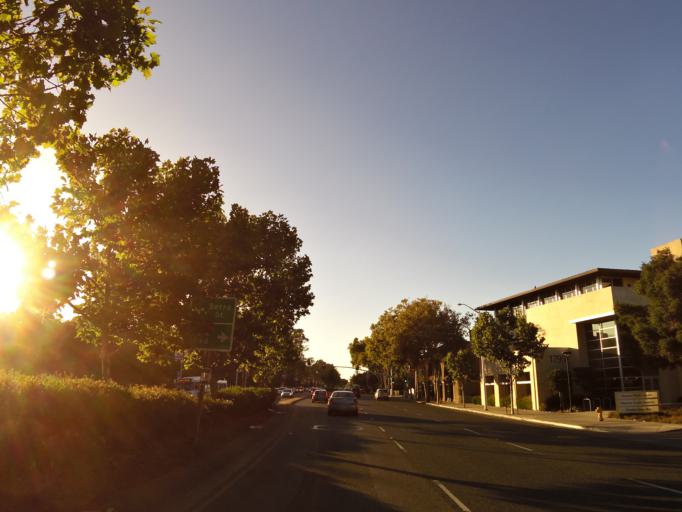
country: US
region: California
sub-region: Santa Clara County
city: Palo Alto
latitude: 37.4292
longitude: -122.1508
